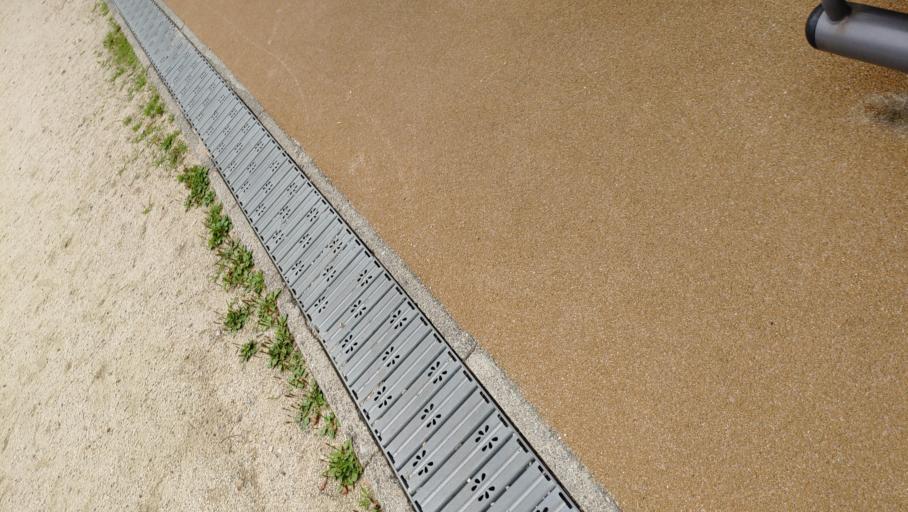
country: KR
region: Gyeonggi-do
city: Seongnam-si
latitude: 37.4900
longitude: 127.0771
